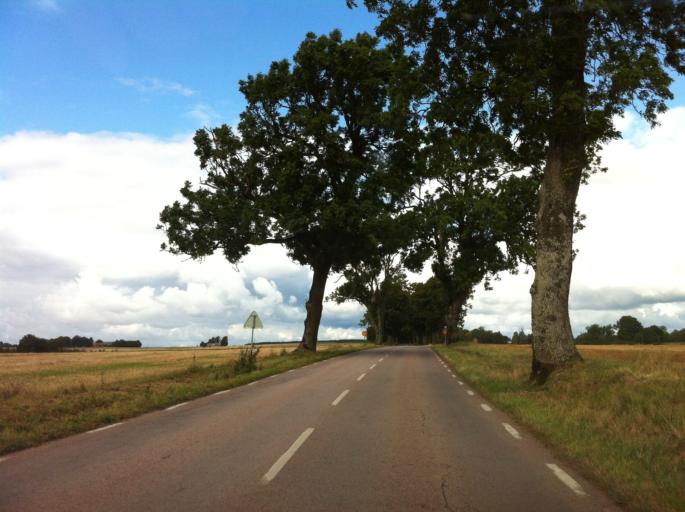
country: SE
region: Skane
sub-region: Eslovs Kommun
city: Eslov
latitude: 55.8686
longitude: 13.2439
